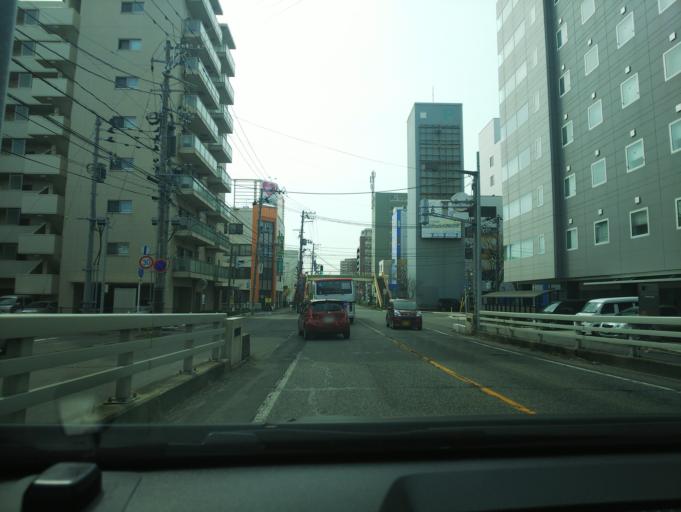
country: JP
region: Niigata
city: Niigata-shi
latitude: 37.9119
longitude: 139.0677
